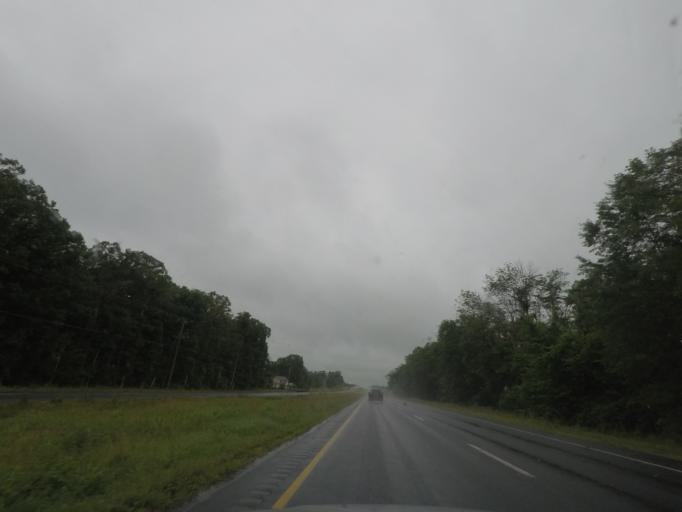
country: US
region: Virginia
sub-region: Fauquier County
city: Bealeton
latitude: 38.6047
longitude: -77.8002
